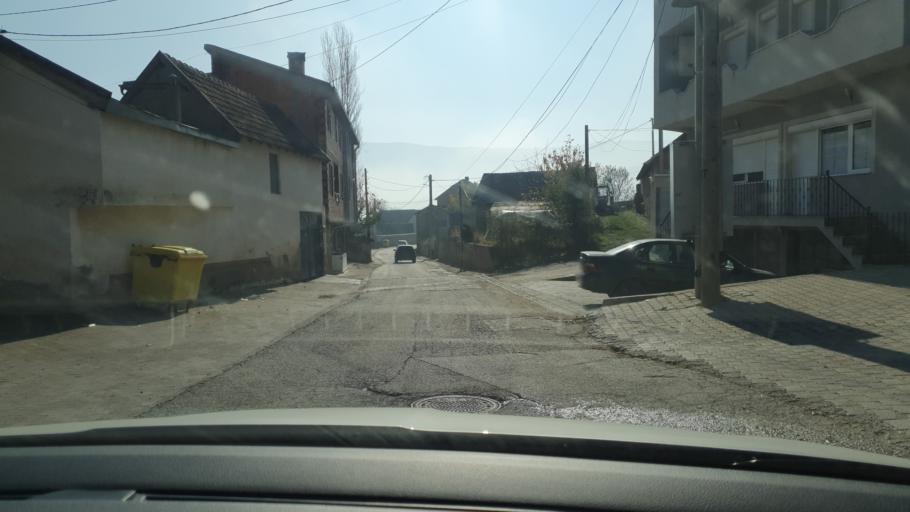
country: MK
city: Bojane
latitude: 41.9996
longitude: 21.1925
